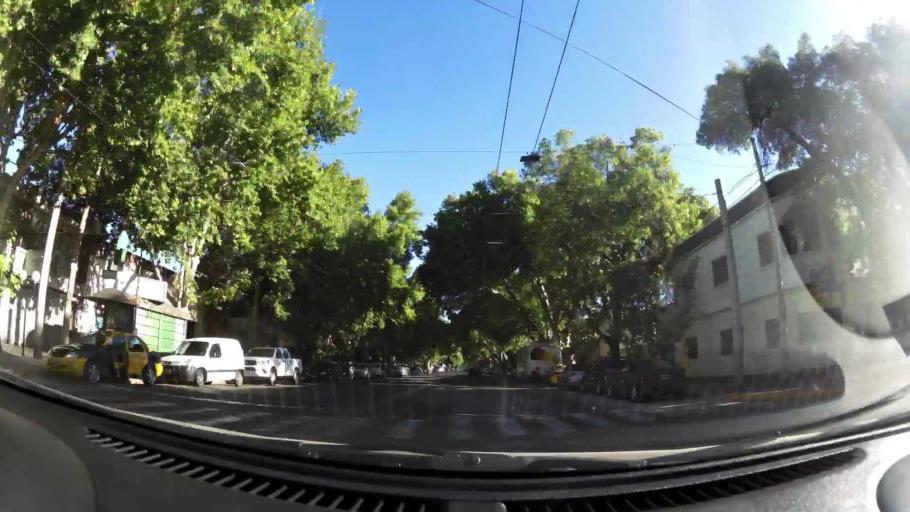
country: AR
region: Mendoza
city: Las Heras
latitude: -32.8717
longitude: -68.8345
